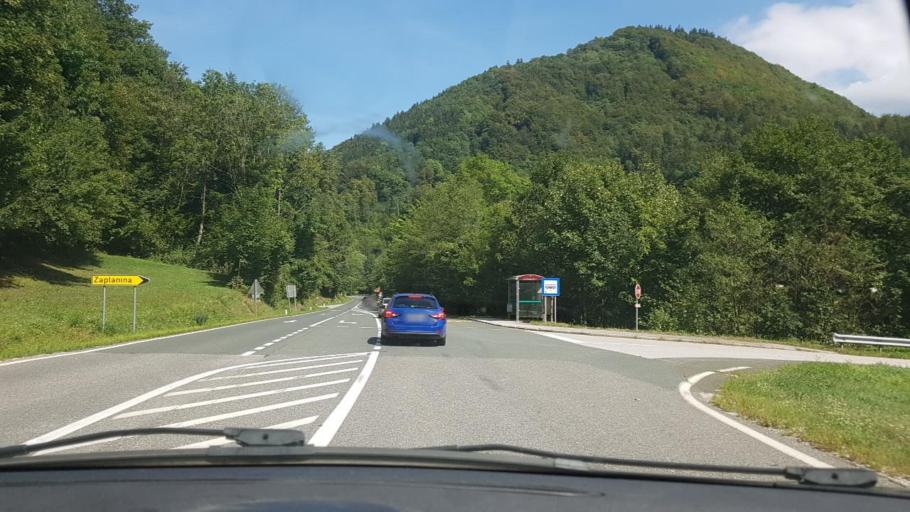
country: SI
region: Vransko
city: Vransko
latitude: 46.2201
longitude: 14.9380
